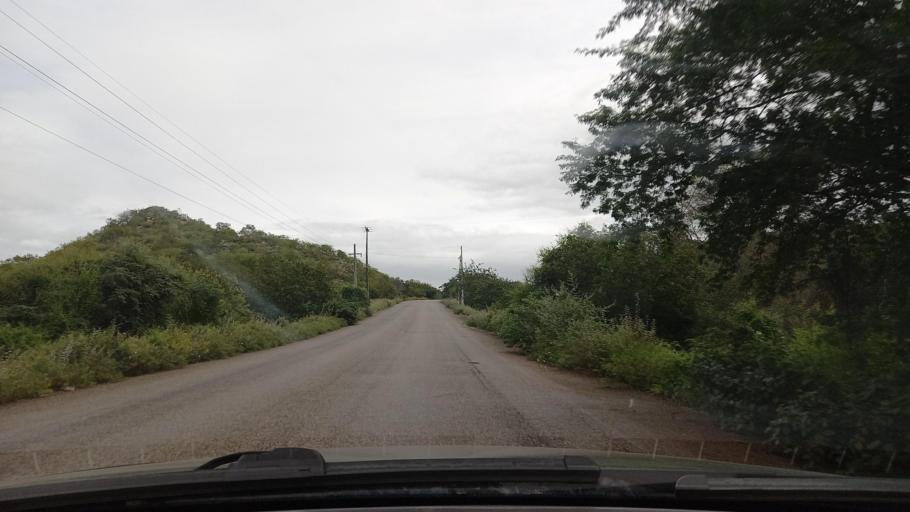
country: BR
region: Sergipe
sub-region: Caninde De Sao Francisco
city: Caninde de Sao Francisco
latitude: -9.6325
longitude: -37.7791
